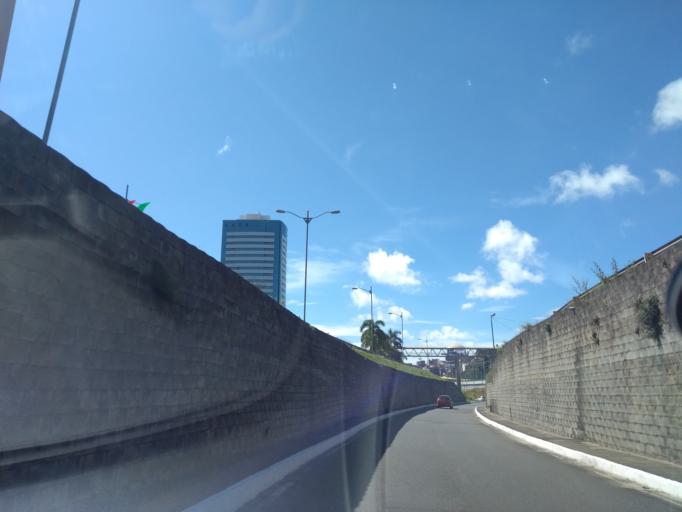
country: BR
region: Bahia
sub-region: Salvador
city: Salvador
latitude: -12.9774
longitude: -38.4543
